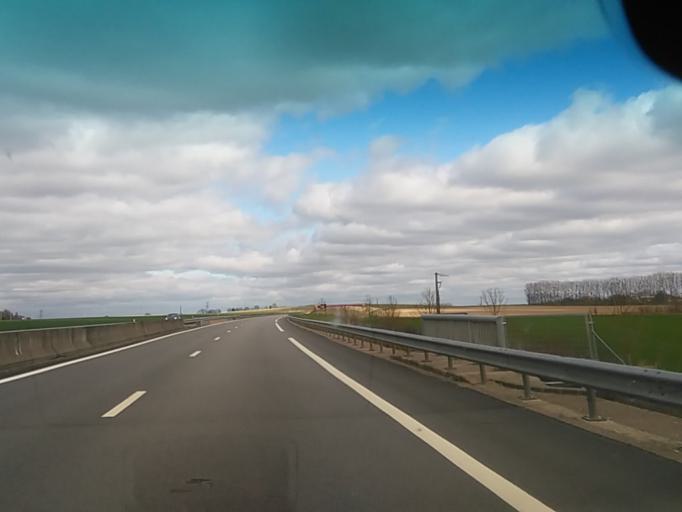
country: FR
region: Haute-Normandie
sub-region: Departement de l'Eure
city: Bourg-Achard
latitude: 49.2974
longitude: 0.7917
